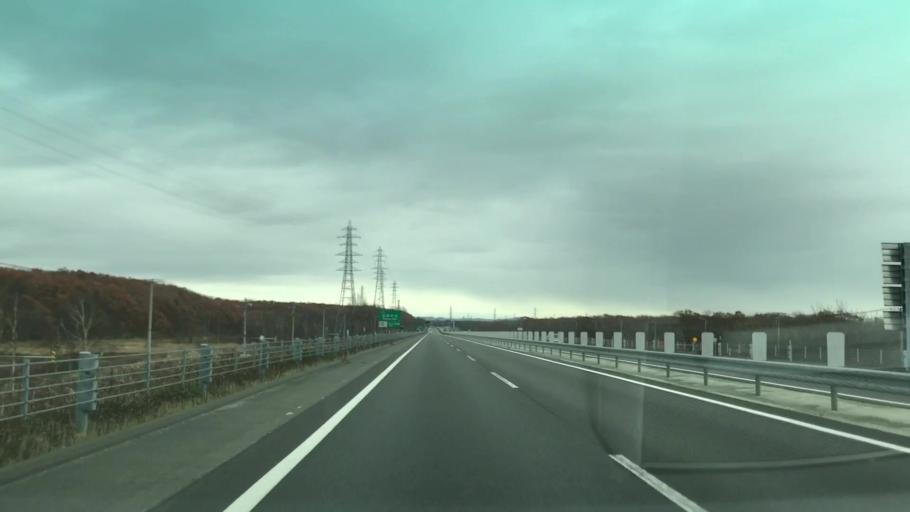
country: JP
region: Hokkaido
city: Tomakomai
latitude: 42.6733
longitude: 141.7678
